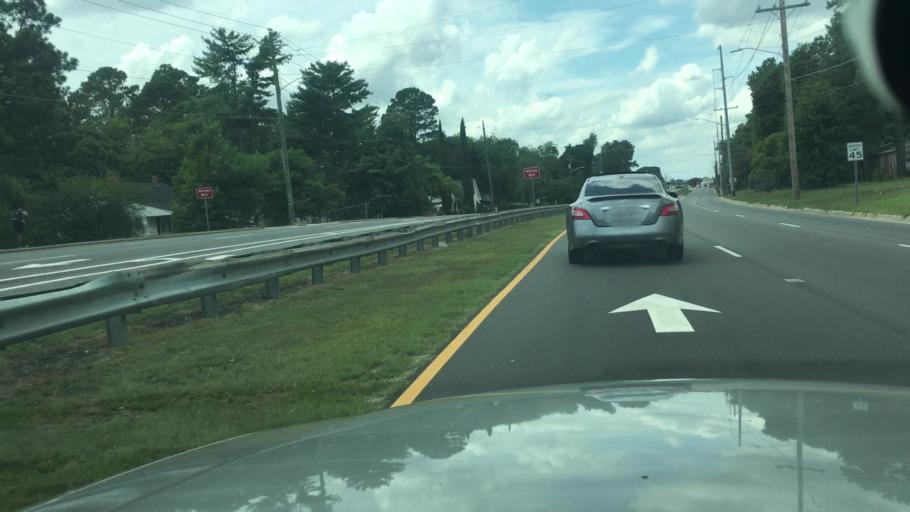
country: US
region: North Carolina
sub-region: Cumberland County
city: Fayetteville
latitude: 35.0700
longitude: -78.9171
